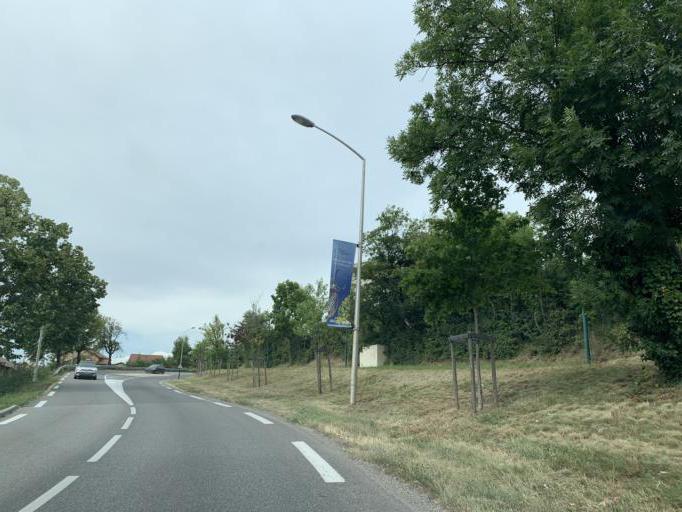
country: FR
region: Provence-Alpes-Cote d'Azur
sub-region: Departement des Hautes-Alpes
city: Gap
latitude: 44.5571
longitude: 6.0627
